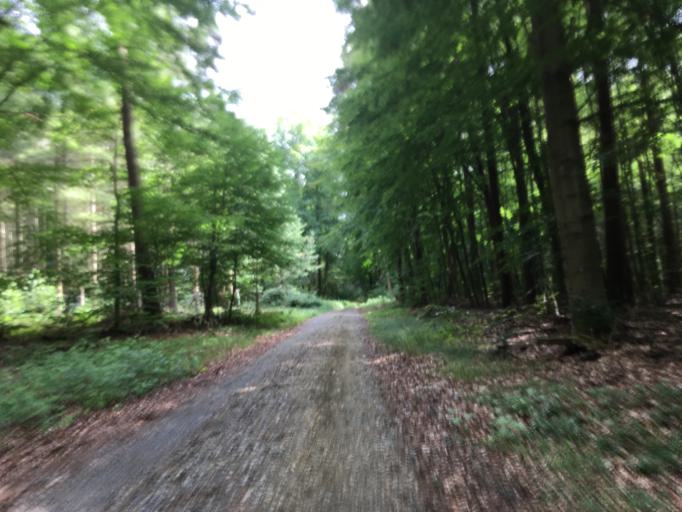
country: DE
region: Brandenburg
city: Bernau bei Berlin
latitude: 52.7372
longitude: 13.5481
